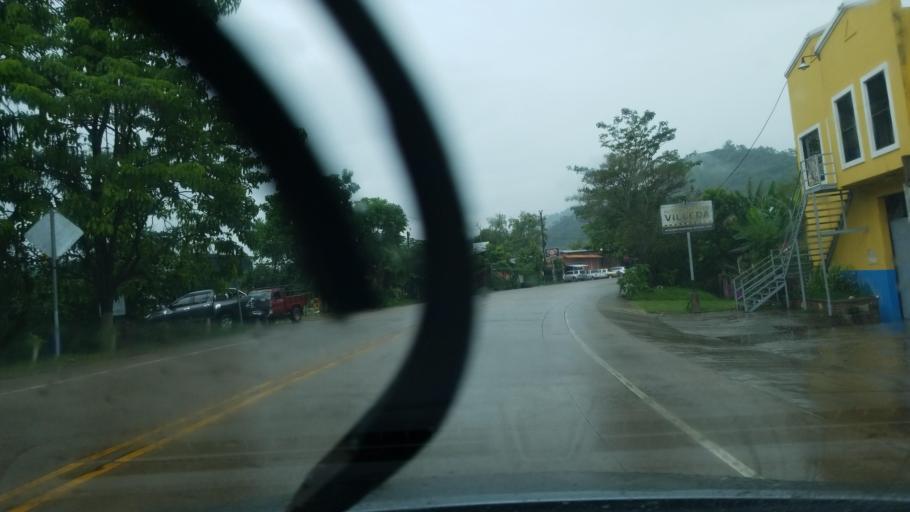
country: HN
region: Copan
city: Copan
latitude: 14.8343
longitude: -89.1586
